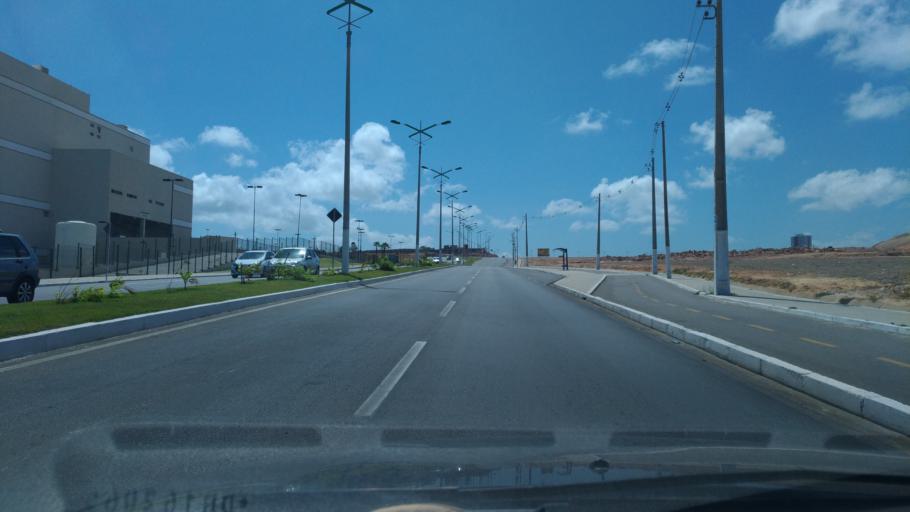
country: BR
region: Alagoas
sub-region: Maceio
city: Maceio
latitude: -9.6258
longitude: -35.6982
